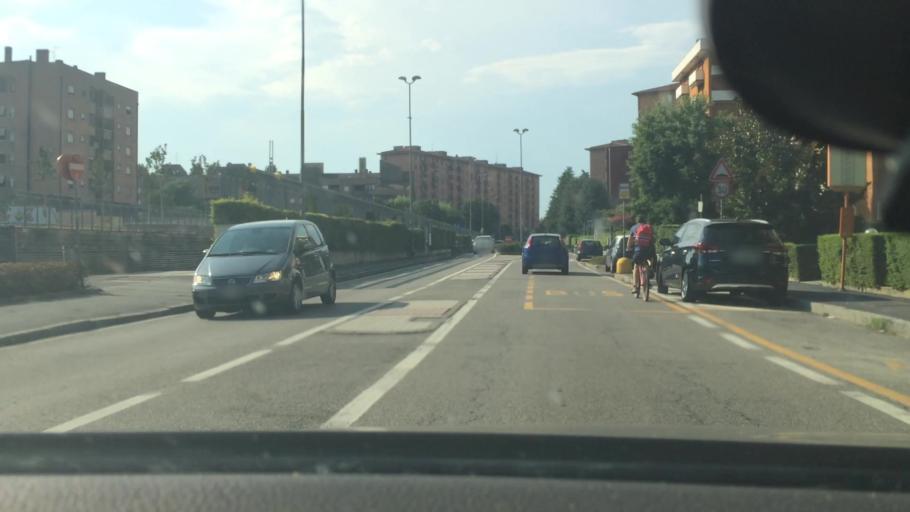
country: IT
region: Lombardy
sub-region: Citta metropolitana di Milano
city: Settimo Milanese
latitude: 45.4811
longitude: 9.0595
